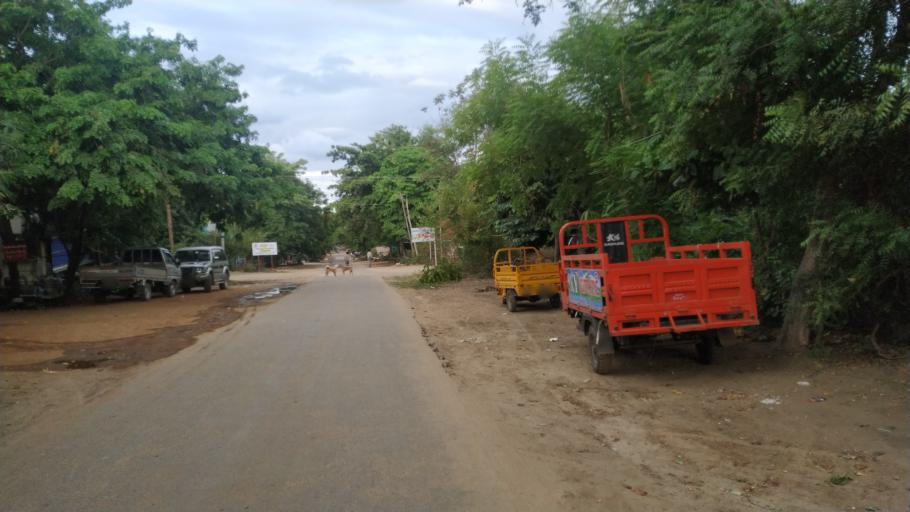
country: MM
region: Magway
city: Pakokku
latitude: 21.3345
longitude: 95.0708
